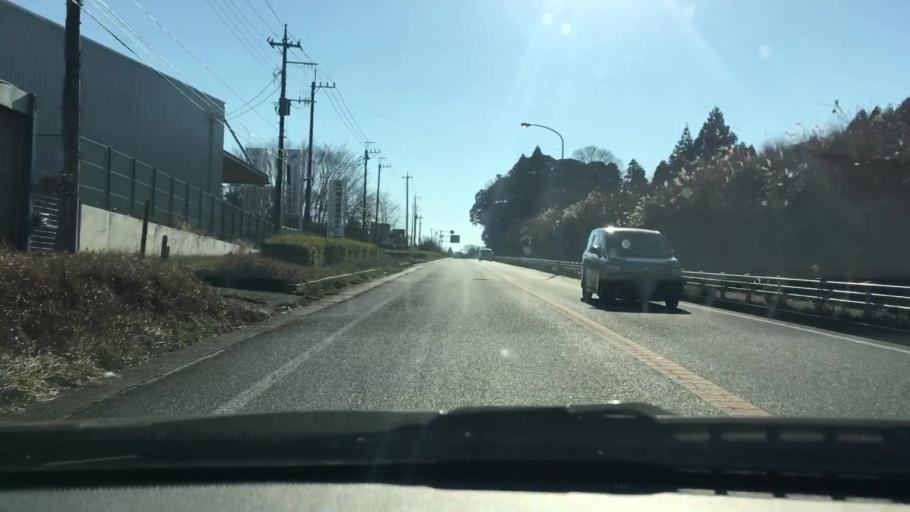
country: JP
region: Chiba
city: Sakura
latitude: 35.6927
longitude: 140.2451
